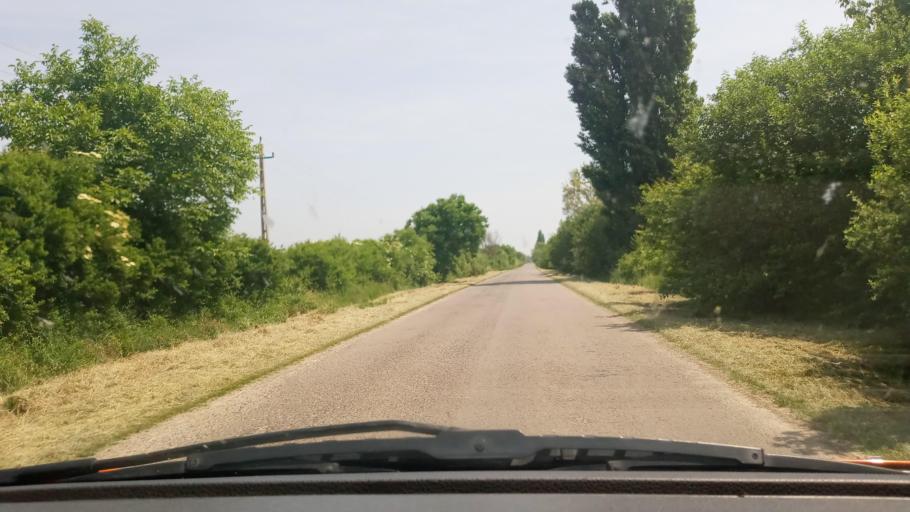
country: HU
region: Baranya
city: Szigetvar
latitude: 45.9661
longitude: 17.6893
